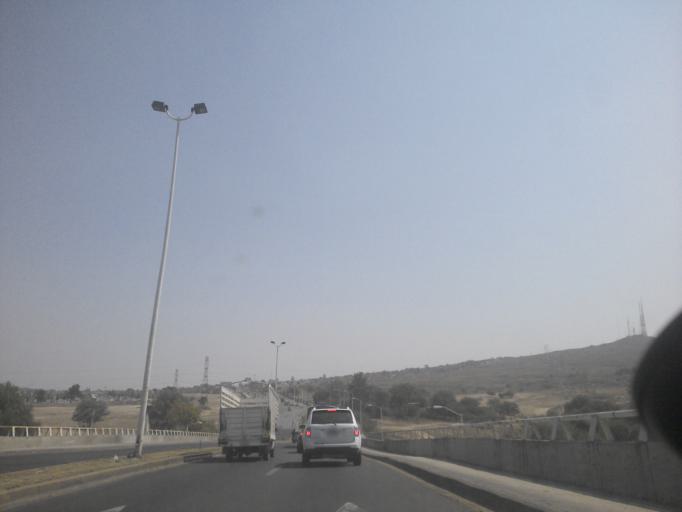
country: MX
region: Jalisco
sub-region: Tlajomulco de Zuniga
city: Altus Bosques
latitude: 20.5880
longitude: -103.3832
